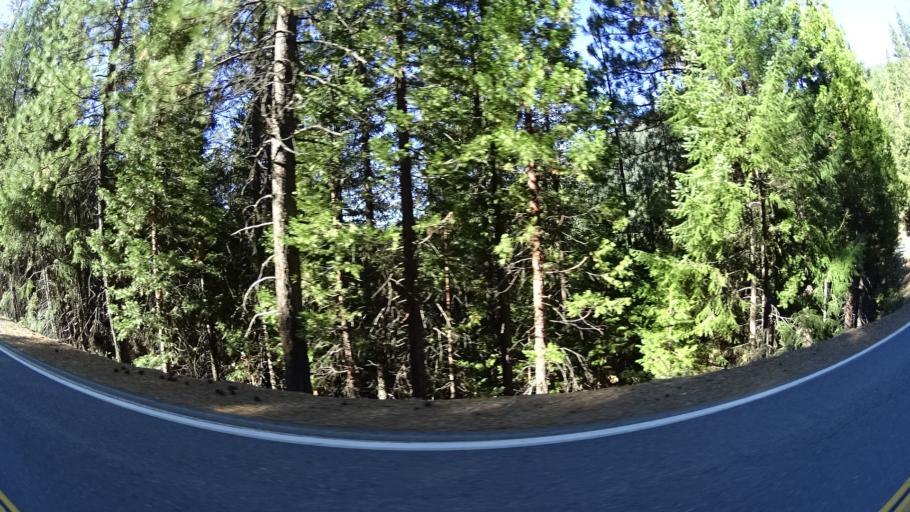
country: US
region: California
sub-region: Trinity County
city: Weaverville
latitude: 41.2227
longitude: -123.0133
